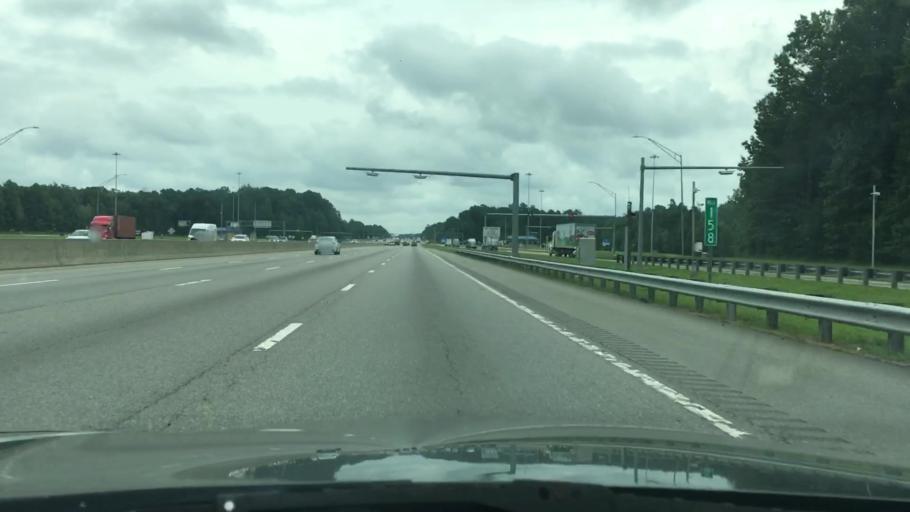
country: US
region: North Carolina
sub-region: Alamance County
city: Mebane
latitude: 36.0774
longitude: -79.2113
